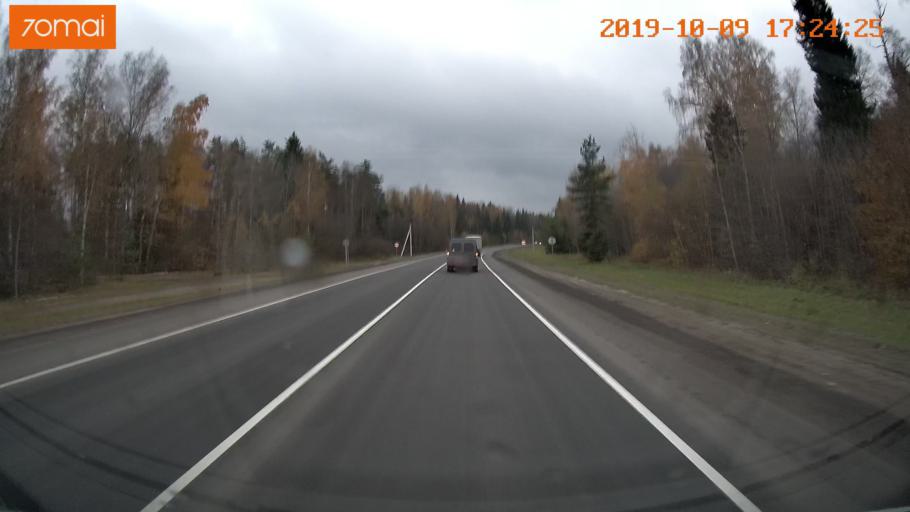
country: RU
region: Ivanovo
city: Furmanov
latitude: 57.1855
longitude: 41.1074
